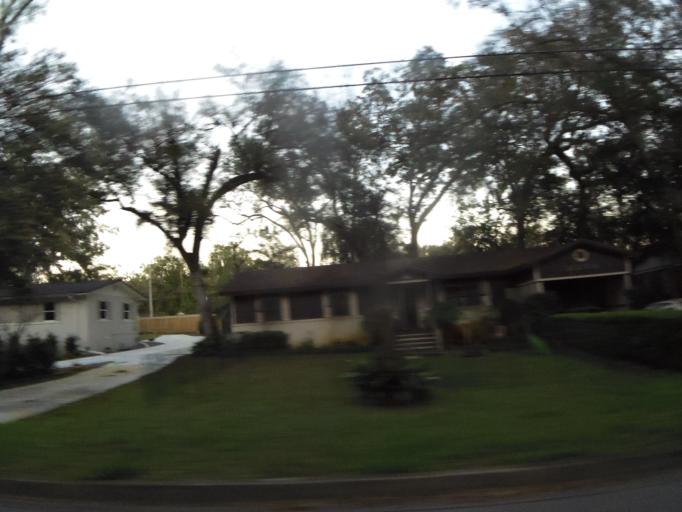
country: US
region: Florida
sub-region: Clay County
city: Orange Park
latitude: 30.1562
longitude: -81.7016
